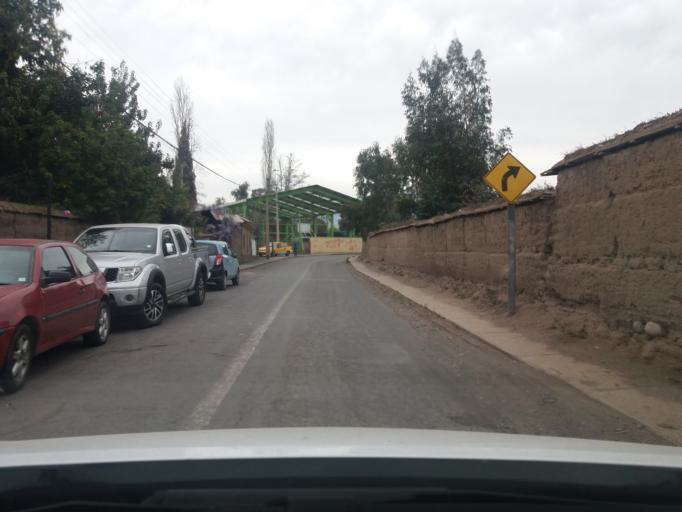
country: CL
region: Valparaiso
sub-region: Provincia de Los Andes
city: Los Andes
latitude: -32.8438
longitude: -70.6309
